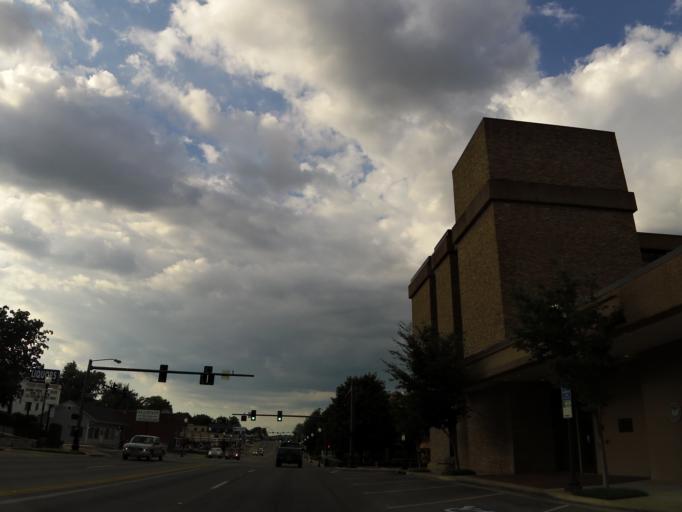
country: US
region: Tennessee
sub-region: Maury County
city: Columbia
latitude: 35.6157
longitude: -87.0354
